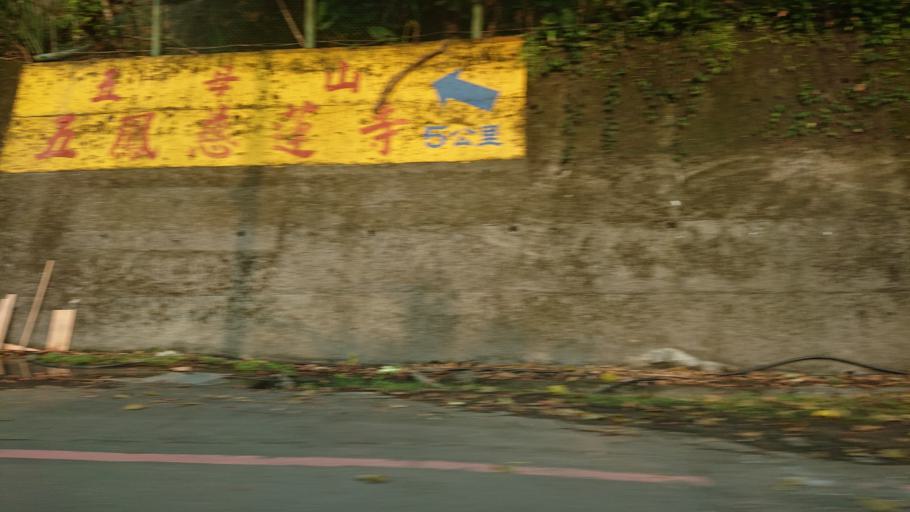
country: TW
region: Taiwan
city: Daxi
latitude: 24.8738
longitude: 121.3894
